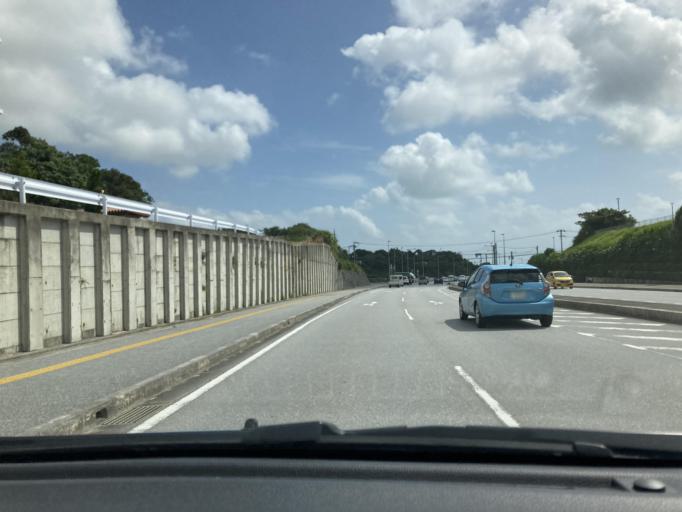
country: JP
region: Okinawa
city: Okinawa
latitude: 26.3164
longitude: 127.7975
